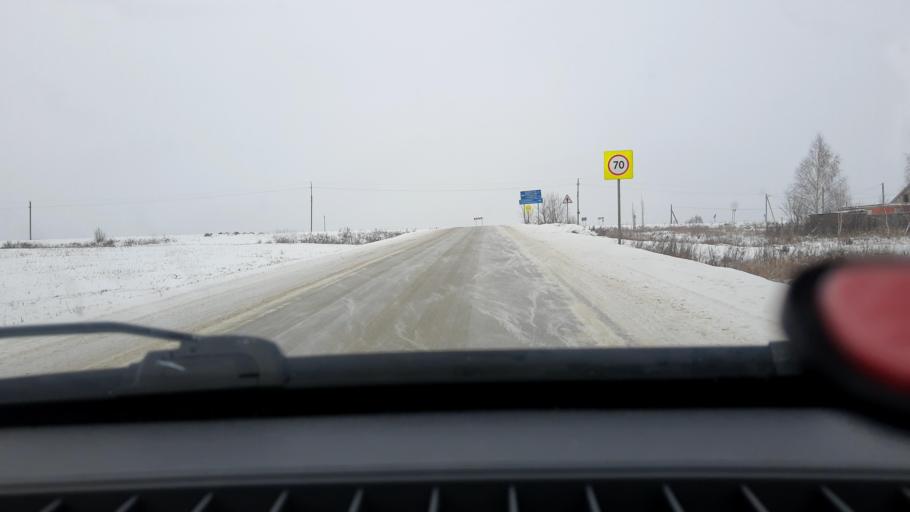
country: RU
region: Bashkortostan
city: Iglino
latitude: 54.7073
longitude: 56.4018
